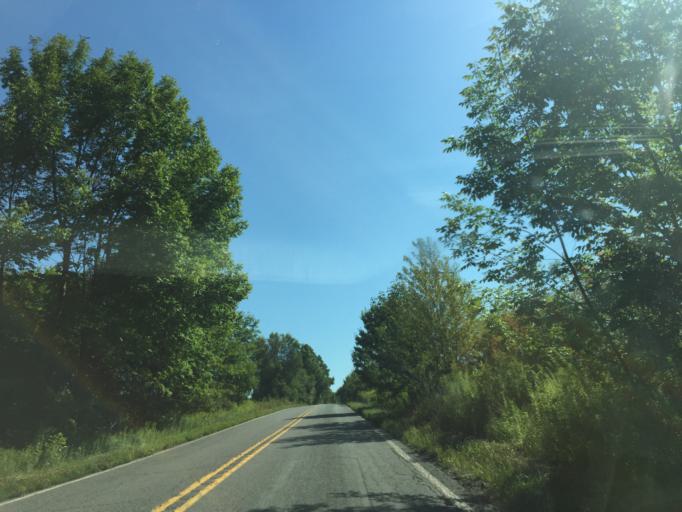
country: US
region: Pennsylvania
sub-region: Wayne County
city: Honesdale
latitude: 41.7189
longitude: -75.2219
